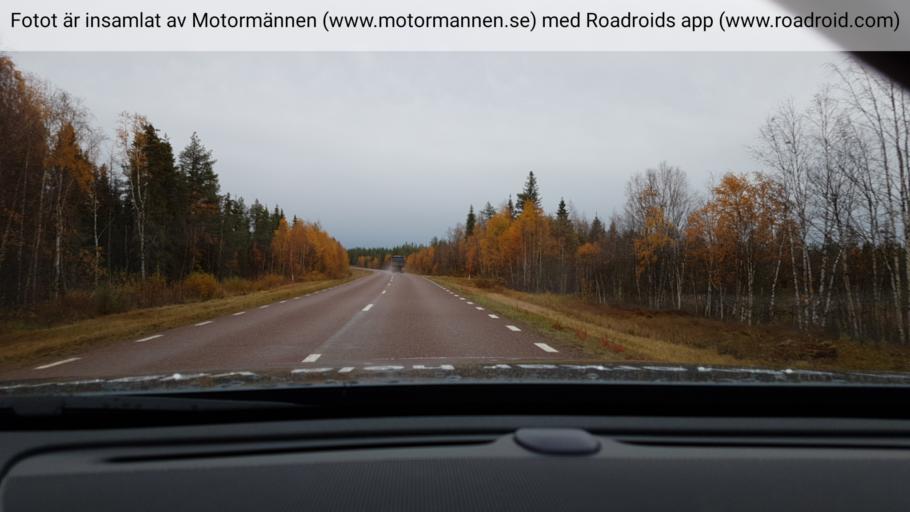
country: SE
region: Norrbotten
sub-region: Pajala Kommun
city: Pajala
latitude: 67.1678
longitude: 22.6612
